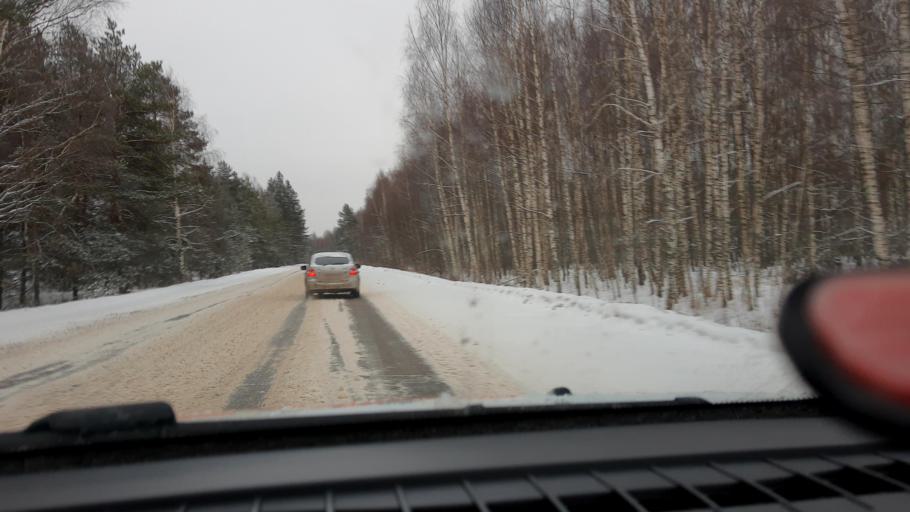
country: RU
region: Nizjnij Novgorod
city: Pamyat' Parizhskoy Kommuny
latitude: 56.2630
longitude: 44.4433
